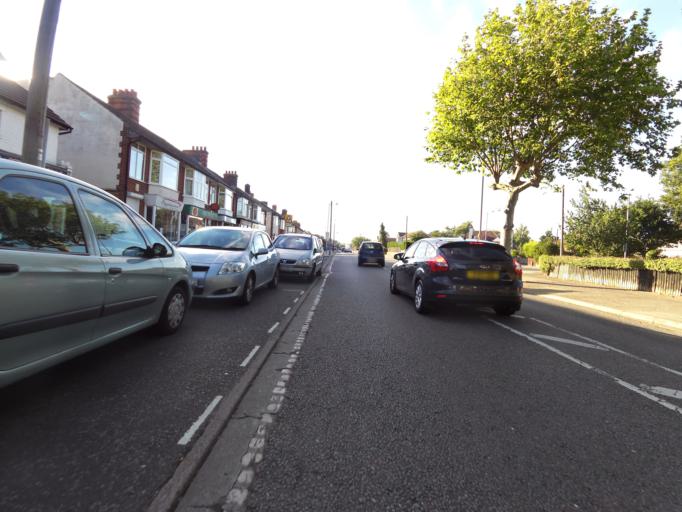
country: GB
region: England
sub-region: Suffolk
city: Ipswich
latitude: 52.0404
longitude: 1.1855
